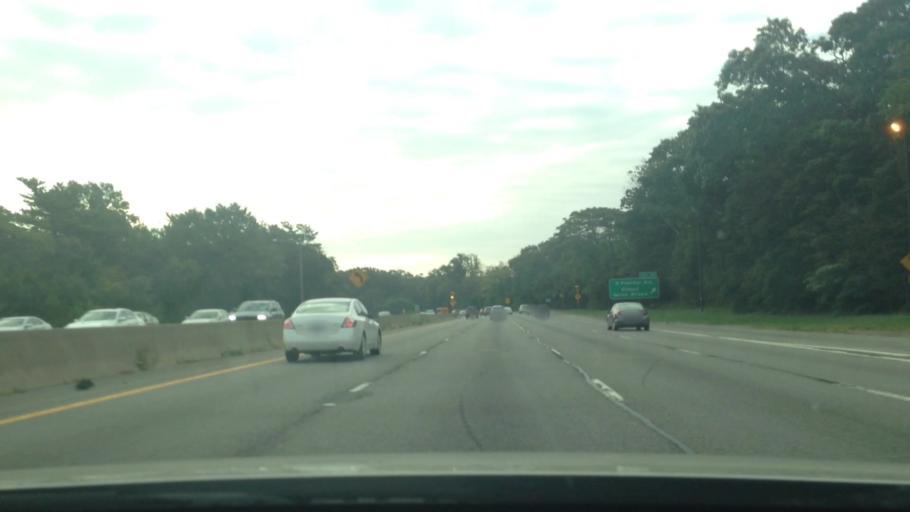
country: US
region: New York
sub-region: Nassau County
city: North Valley Stream
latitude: 40.6813
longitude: -73.7047
